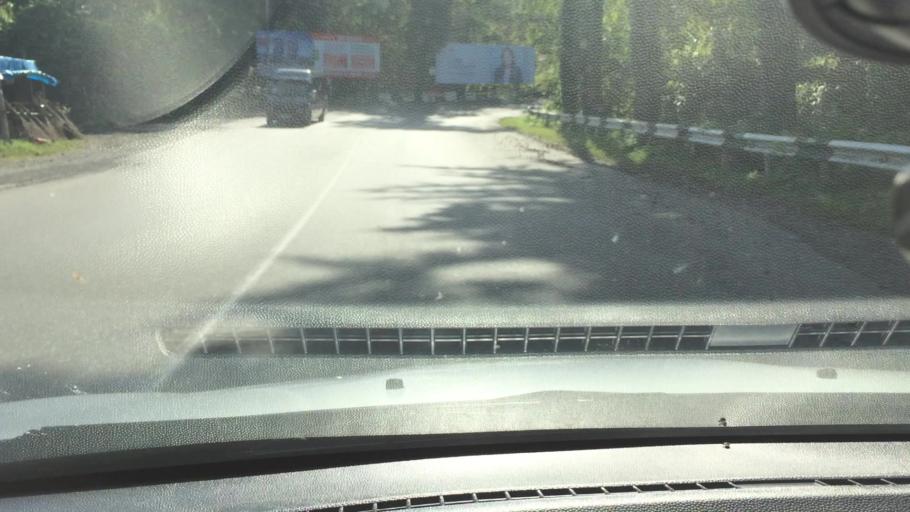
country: GE
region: Ajaria
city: Kobuleti
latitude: 41.7651
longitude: 41.7549
